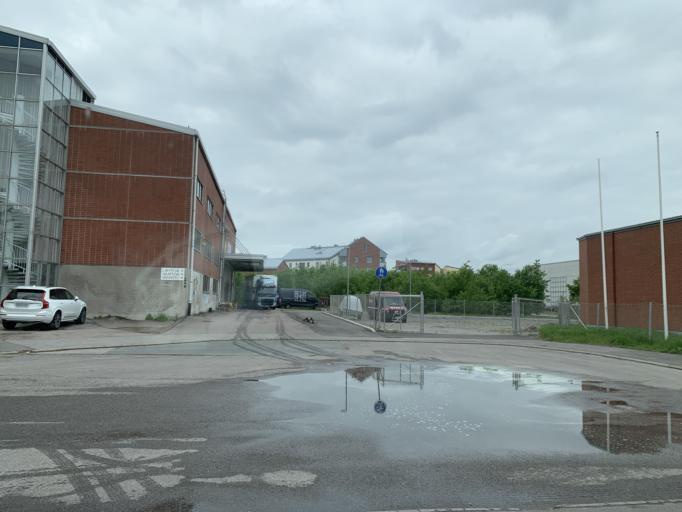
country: FI
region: Uusimaa
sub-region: Helsinki
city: Vantaa
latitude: 60.2525
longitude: 25.0258
